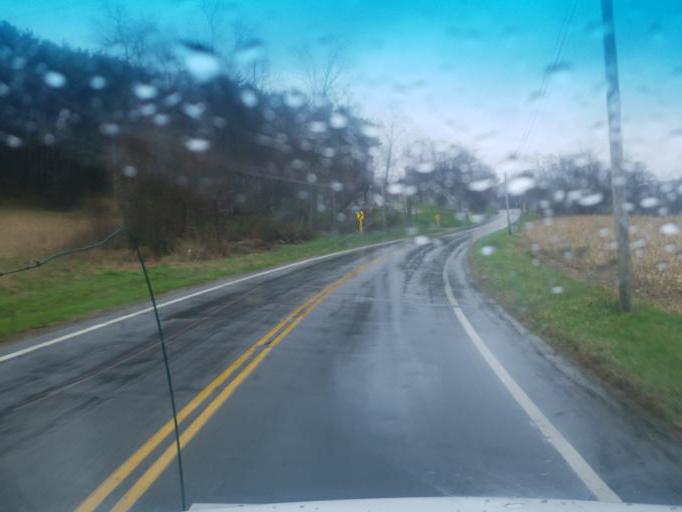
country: US
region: Ohio
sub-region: Holmes County
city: Millersburg
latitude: 40.4820
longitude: -82.0322
